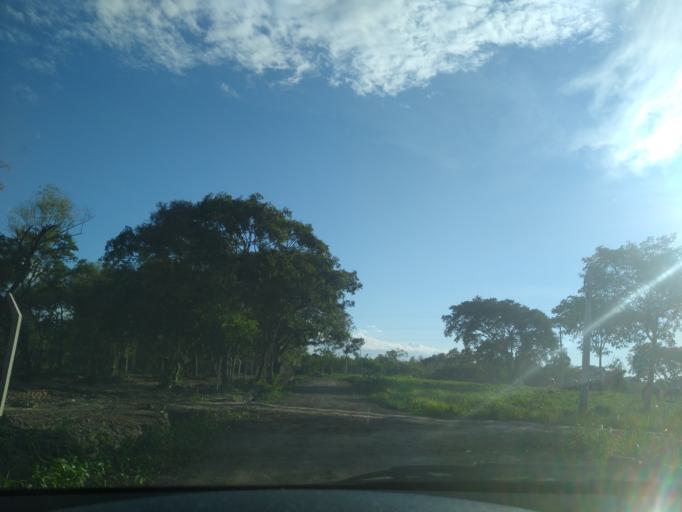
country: AR
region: Chaco
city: Resistencia
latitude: -27.4415
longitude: -58.9521
